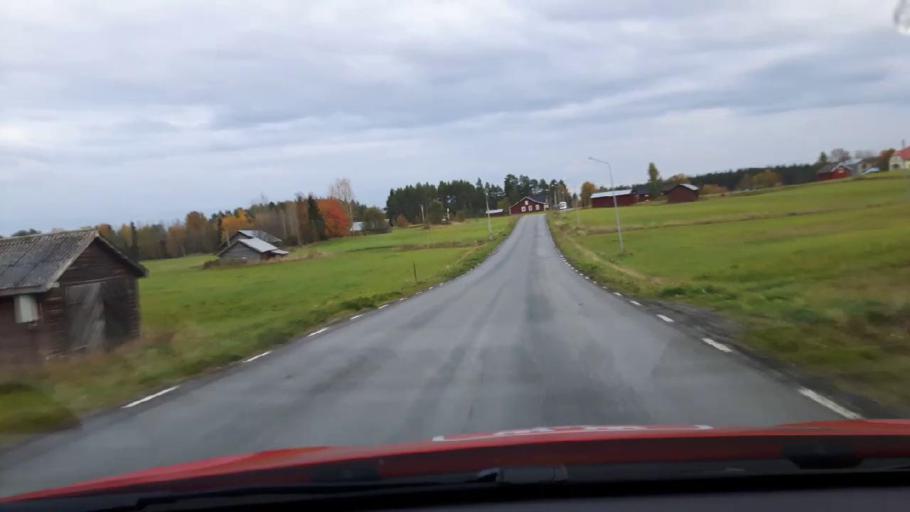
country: SE
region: Jaemtland
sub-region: OEstersunds Kommun
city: Lit
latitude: 63.3122
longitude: 14.9916
